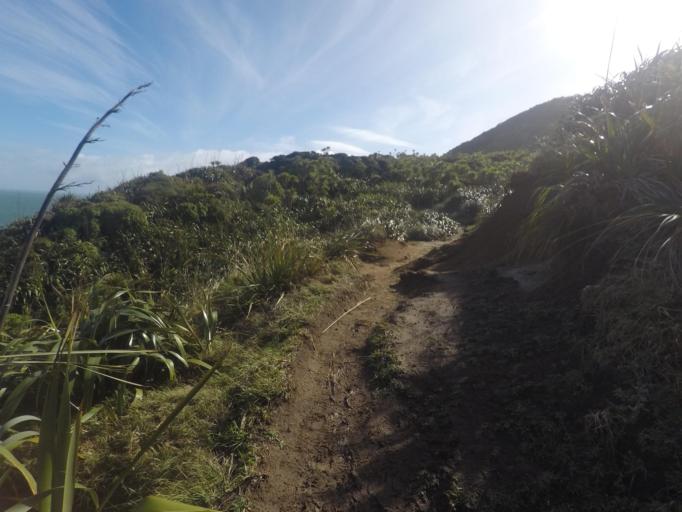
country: NZ
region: Auckland
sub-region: Auckland
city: Muriwai Beach
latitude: -36.8607
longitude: 174.4340
